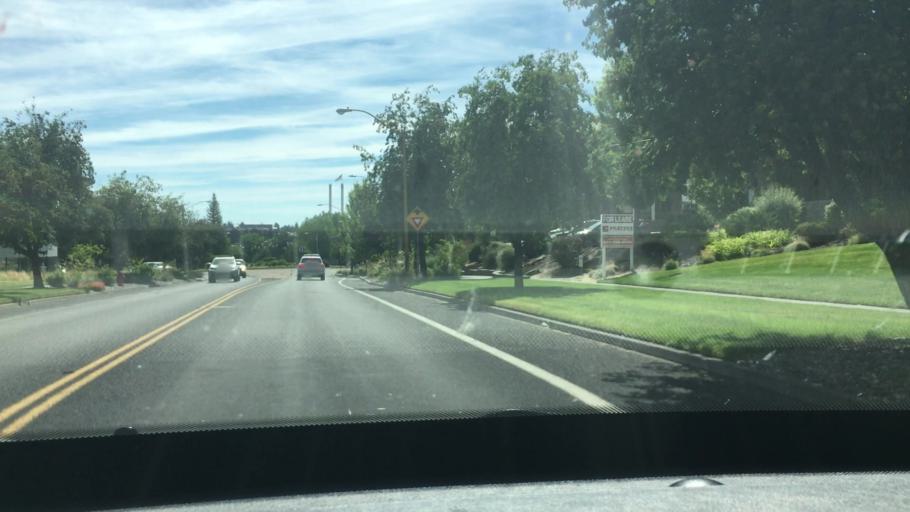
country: US
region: Oregon
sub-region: Deschutes County
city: Bend
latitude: 44.0479
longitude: -121.3247
